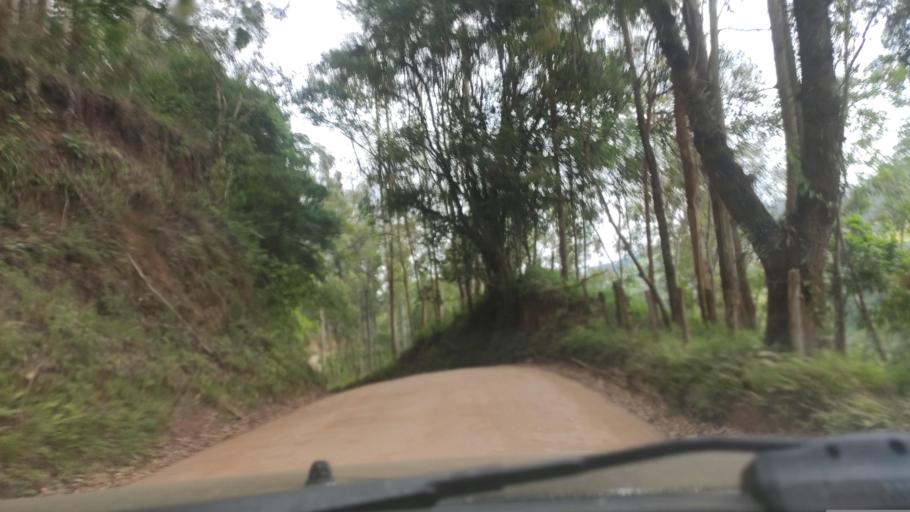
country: BR
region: Minas Gerais
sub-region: Paraisopolis
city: Paraisopolis
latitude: -22.6830
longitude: -45.8530
